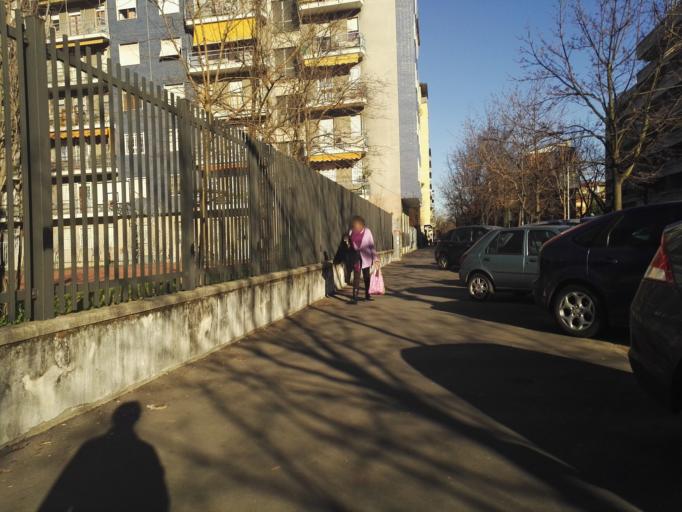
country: IT
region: Lombardy
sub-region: Citta metropolitana di Milano
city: Romano Banco
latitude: 45.4653
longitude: 9.1315
